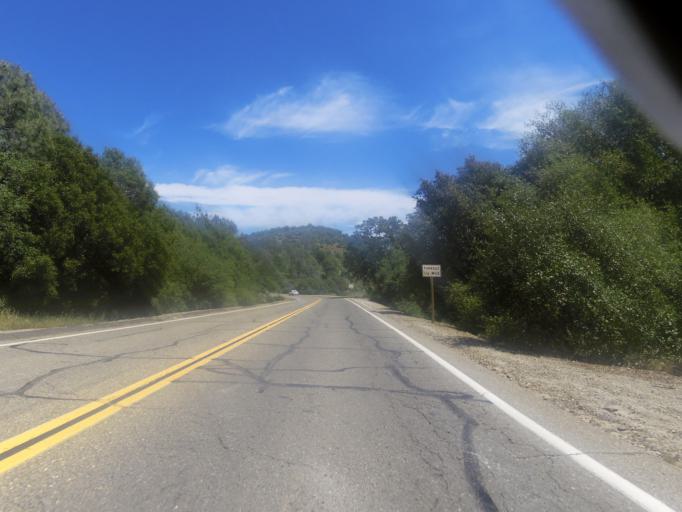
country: US
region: California
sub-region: Mariposa County
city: Mariposa
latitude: 37.5011
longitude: -119.9714
